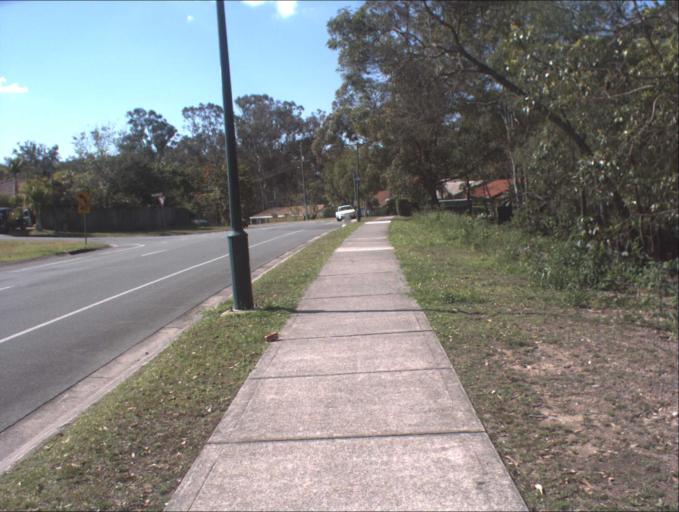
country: AU
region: Queensland
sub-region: Logan
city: Waterford West
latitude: -27.6991
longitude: 153.1612
